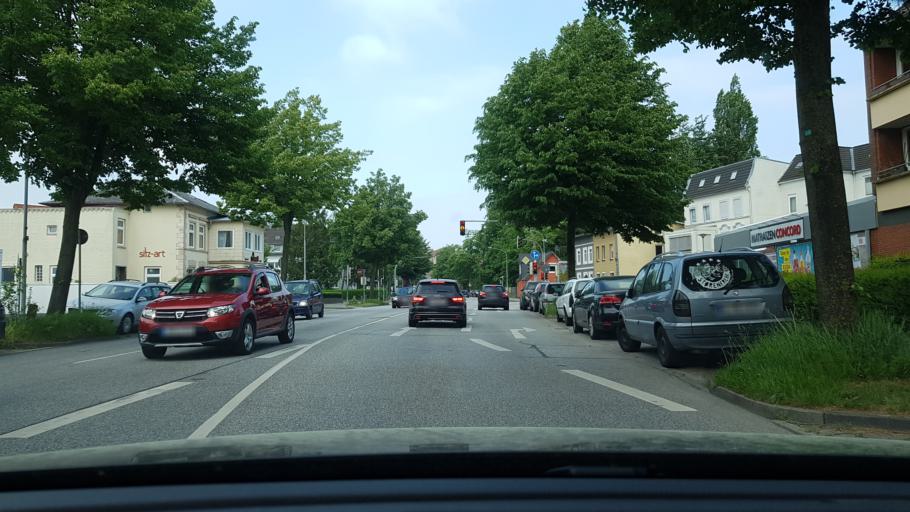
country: DE
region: Schleswig-Holstein
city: Luebeck
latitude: 53.8471
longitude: 10.6846
